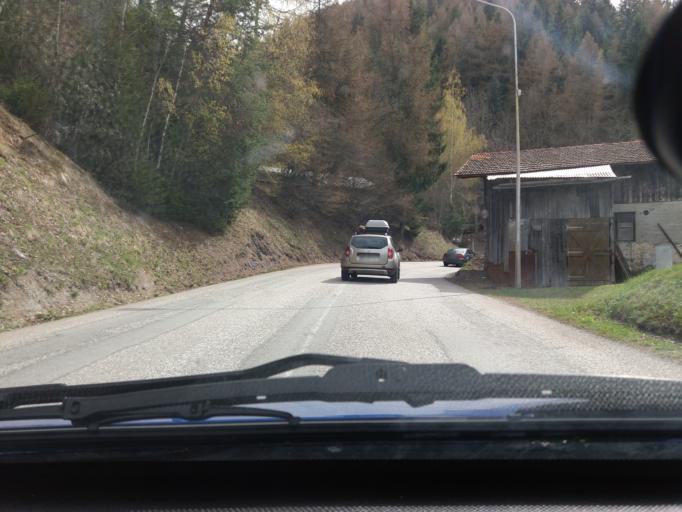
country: FR
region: Rhone-Alpes
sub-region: Departement de la Savoie
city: Macot-la-Plagne
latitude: 45.5513
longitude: 6.6750
